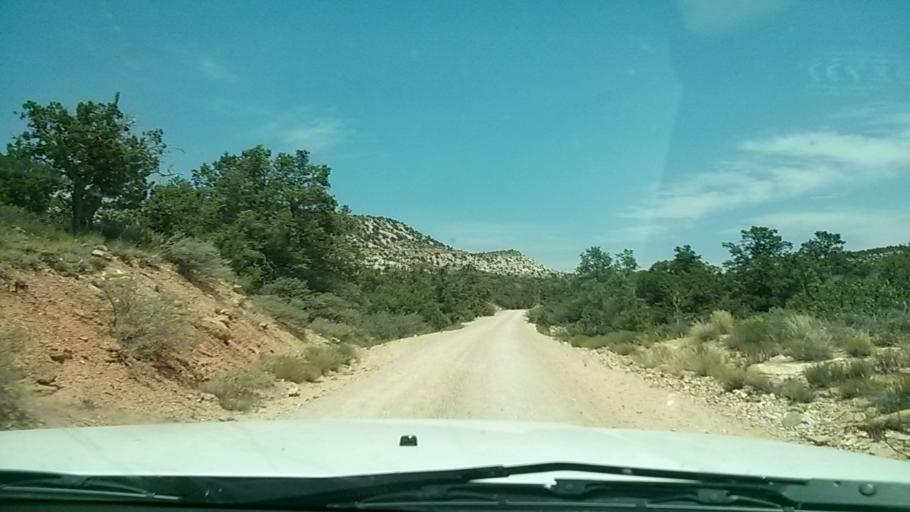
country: US
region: Utah
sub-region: Washington County
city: Toquerville
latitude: 37.2627
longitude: -113.4168
